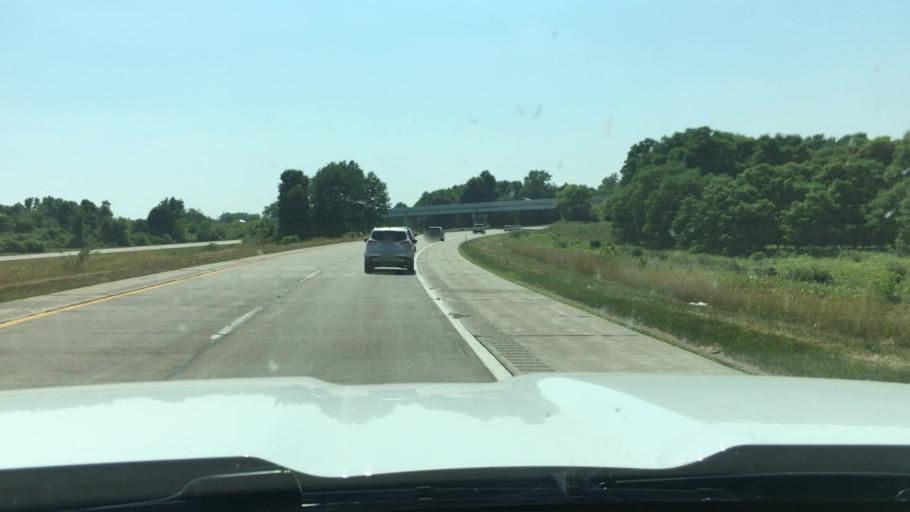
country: US
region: Michigan
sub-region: Clinton County
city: Wacousta
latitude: 42.7888
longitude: -84.6609
